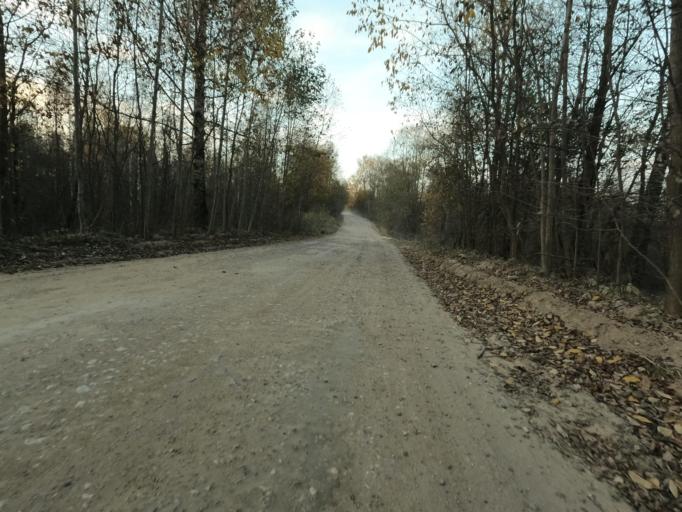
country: RU
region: Leningrad
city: Mga
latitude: 59.7727
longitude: 31.2263
